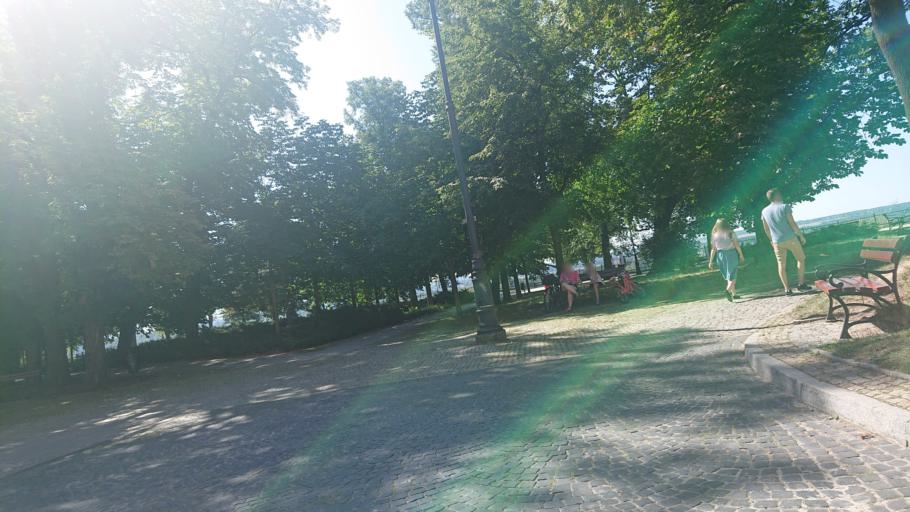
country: PL
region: Masovian Voivodeship
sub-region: Plock
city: Plock
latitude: 52.5411
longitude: 19.6889
